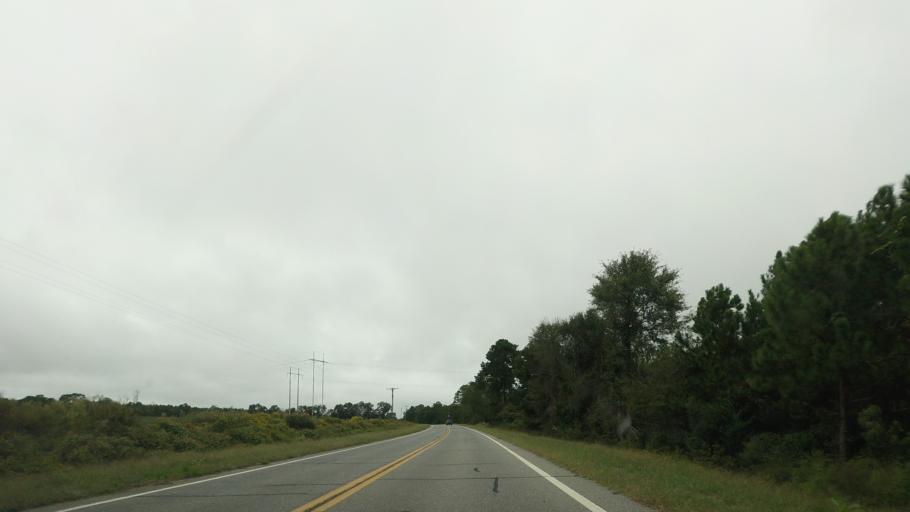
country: US
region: Georgia
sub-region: Irwin County
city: Ocilla
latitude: 31.5349
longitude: -83.2487
